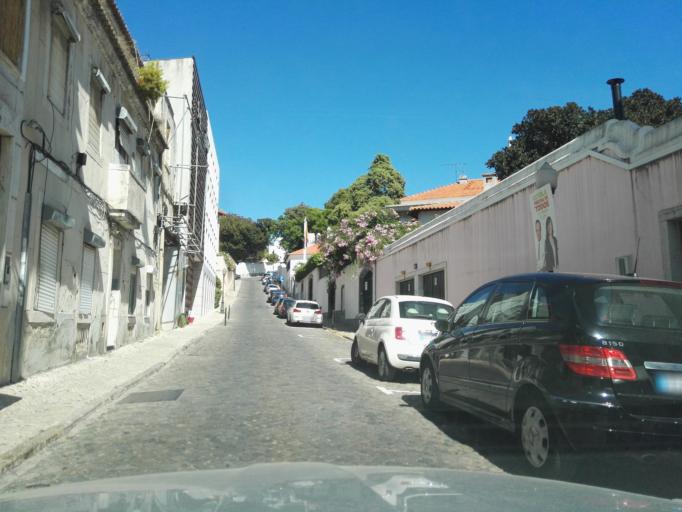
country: PT
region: Setubal
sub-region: Almada
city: Cacilhas
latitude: 38.7081
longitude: -9.1649
